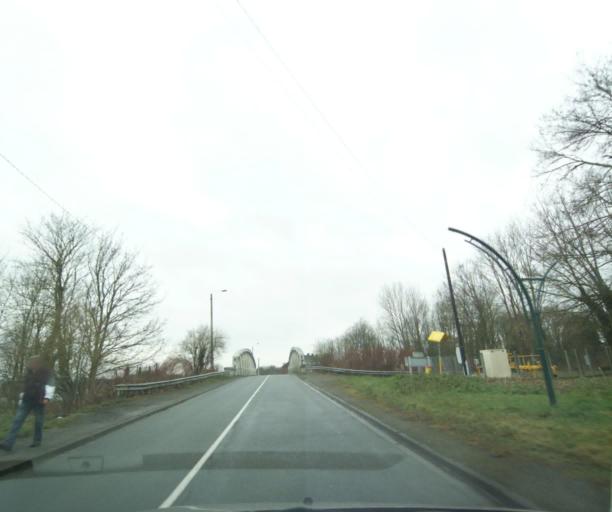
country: FR
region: Nord-Pas-de-Calais
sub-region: Departement du Nord
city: Prouvy
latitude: 50.3136
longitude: 3.4522
